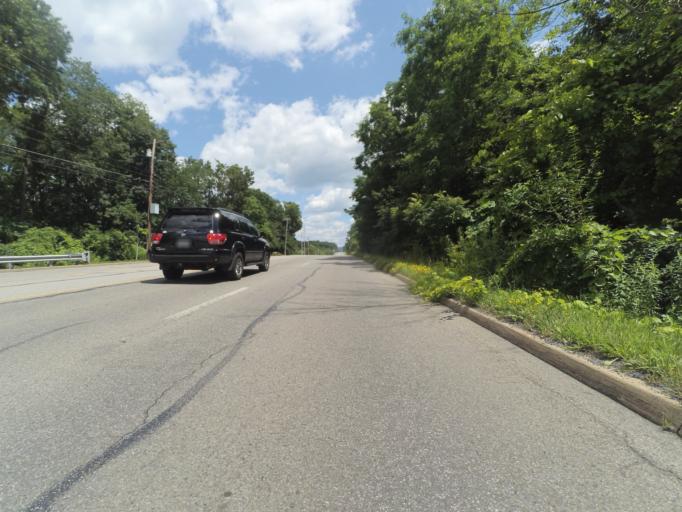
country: US
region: Pennsylvania
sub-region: Centre County
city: Lemont
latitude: 40.7842
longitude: -77.8263
